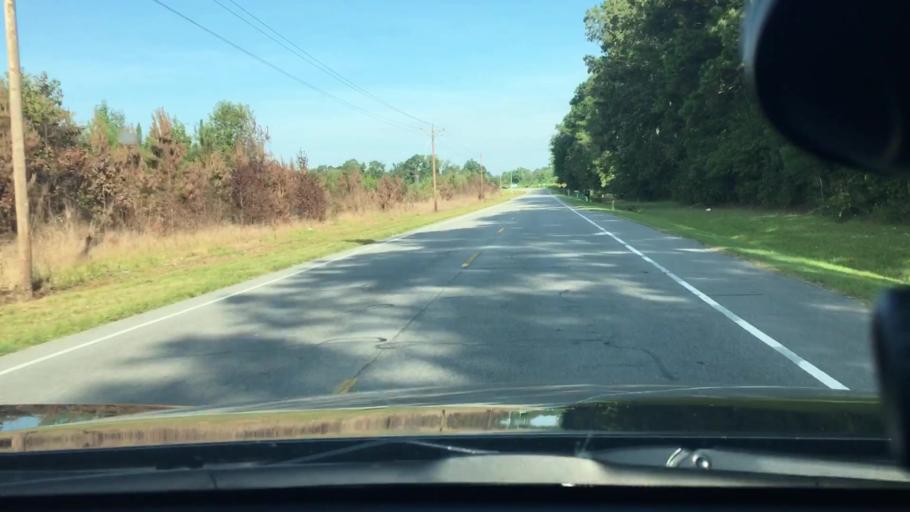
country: US
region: North Carolina
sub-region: Edgecombe County
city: Pinetops
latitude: 35.7866
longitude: -77.6221
